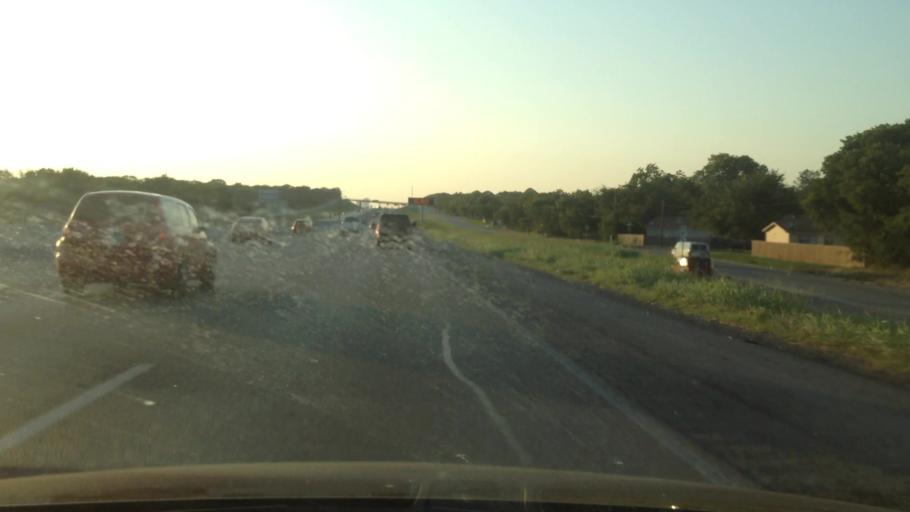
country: US
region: Texas
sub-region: Tarrant County
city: Forest Hill
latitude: 32.7014
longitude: -97.2643
